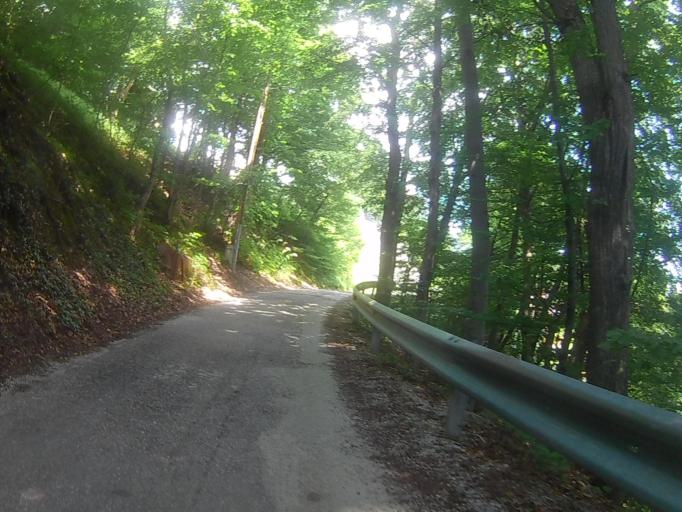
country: SI
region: Maribor
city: Bresternica
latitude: 46.5851
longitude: 15.5926
